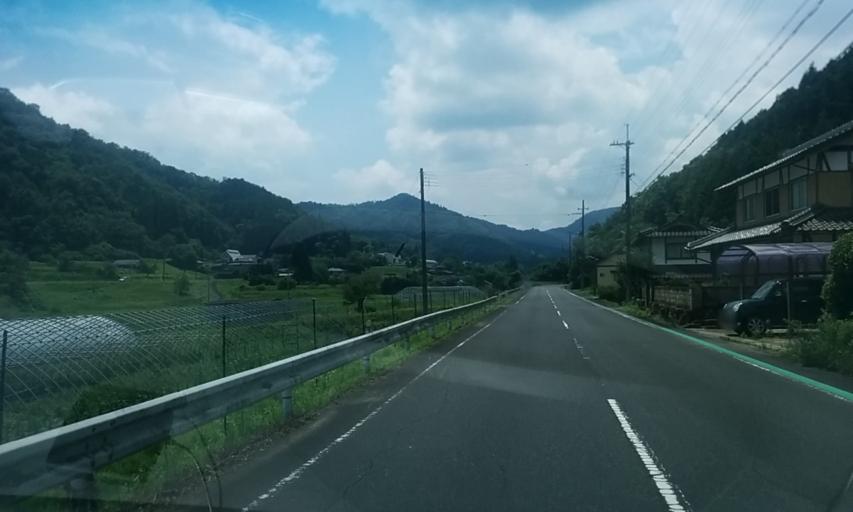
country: JP
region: Kyoto
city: Ayabe
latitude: 35.2081
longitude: 135.2268
